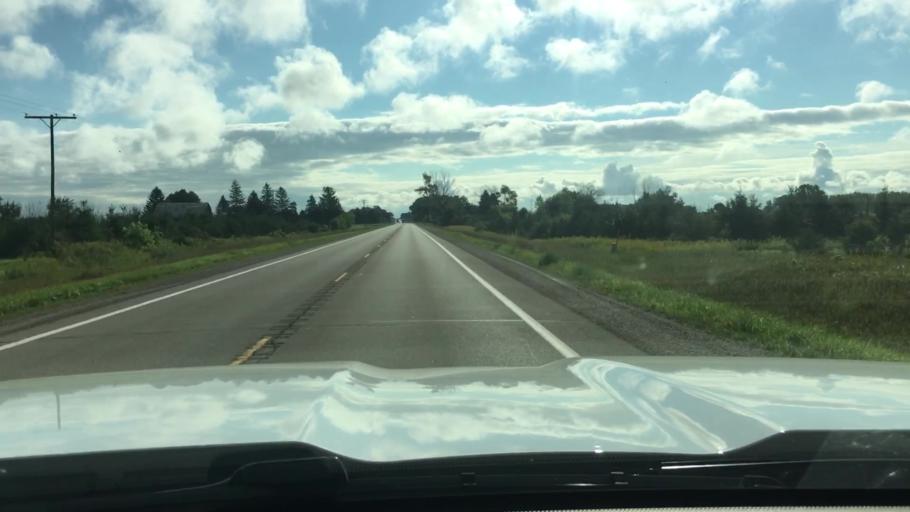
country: US
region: Michigan
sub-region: Tuscola County
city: Cass City
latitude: 43.5995
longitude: -83.2388
